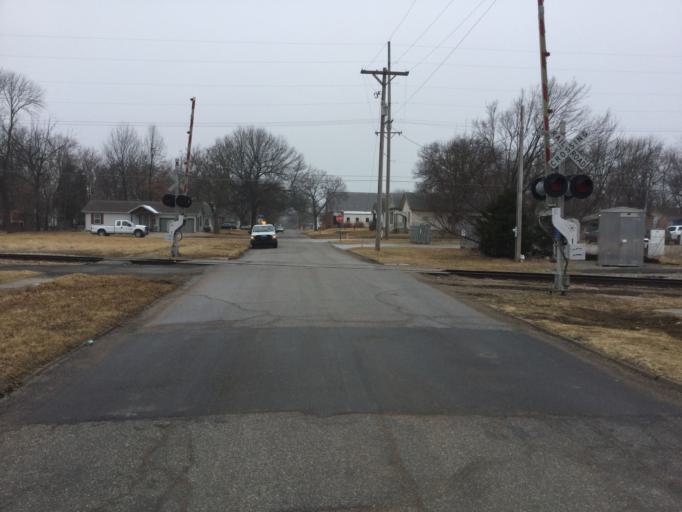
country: US
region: Kansas
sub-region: Crawford County
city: Pittsburg
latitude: 37.4023
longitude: -94.6996
